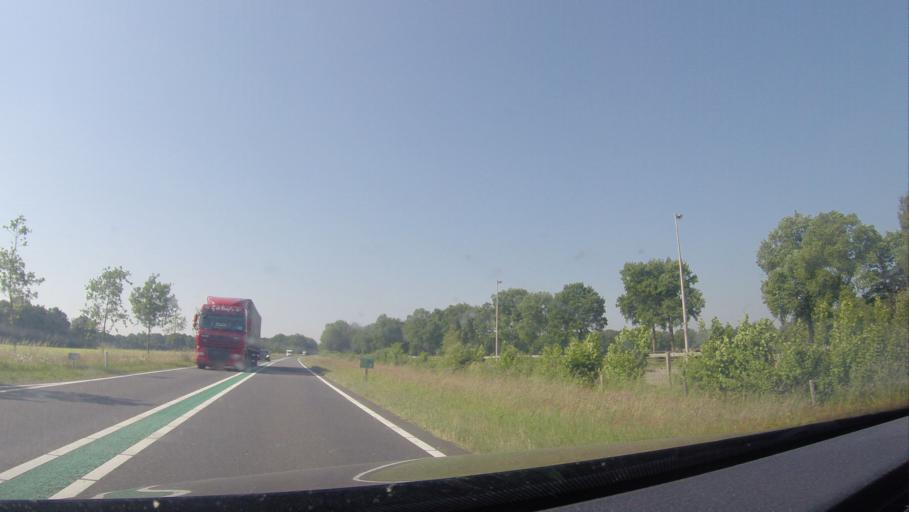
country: NL
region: Gelderland
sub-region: Gemeente Lochem
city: Laren
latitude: 52.2345
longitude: 6.3985
